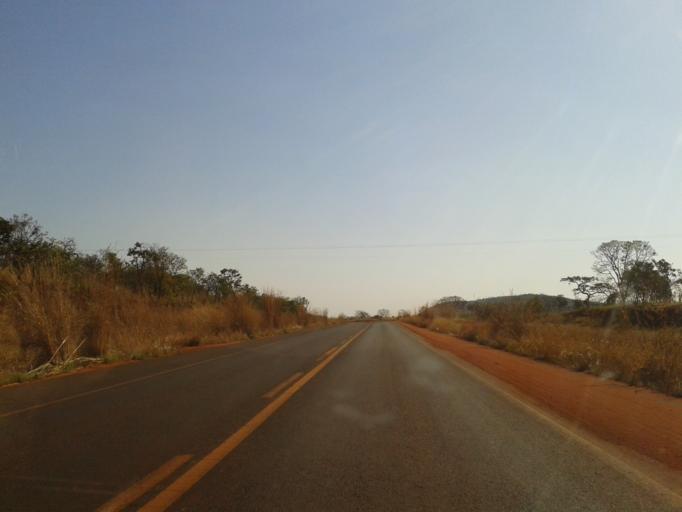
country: BR
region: Minas Gerais
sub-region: Ituiutaba
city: Ituiutaba
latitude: -19.0267
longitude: -49.4996
